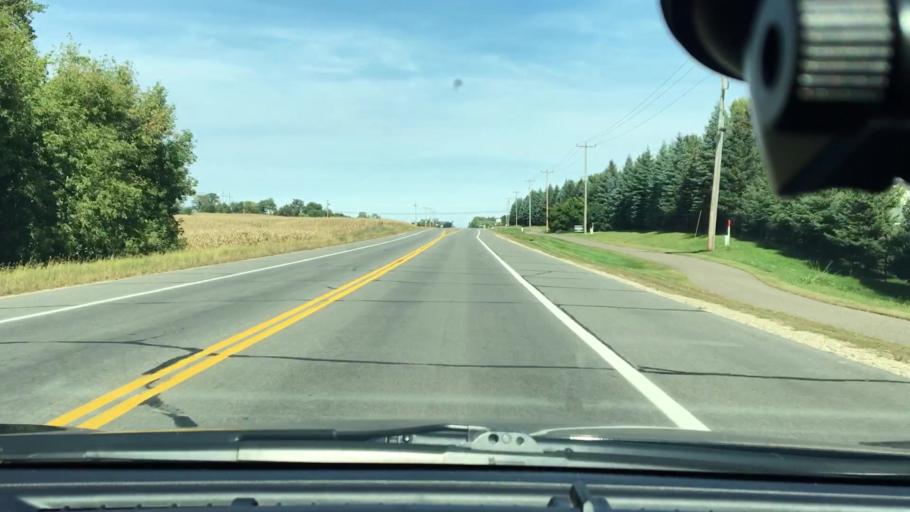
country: US
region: Minnesota
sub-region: Wright County
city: Hanover
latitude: 45.1708
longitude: -93.6657
